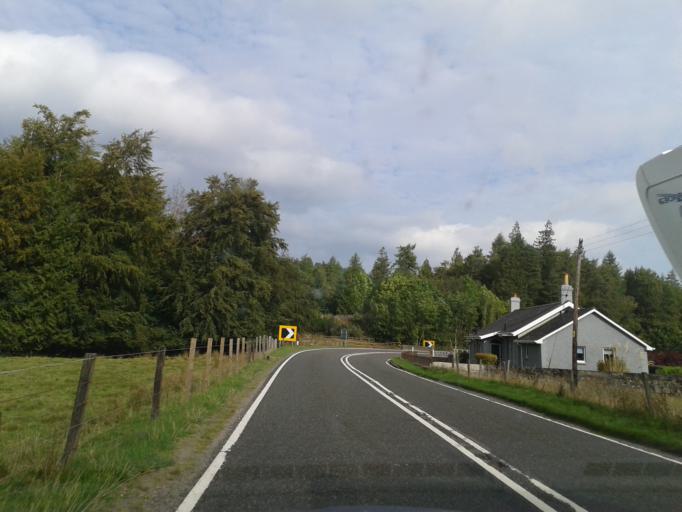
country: GB
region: Scotland
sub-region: Highland
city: Spean Bridge
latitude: 57.0362
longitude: -4.8123
